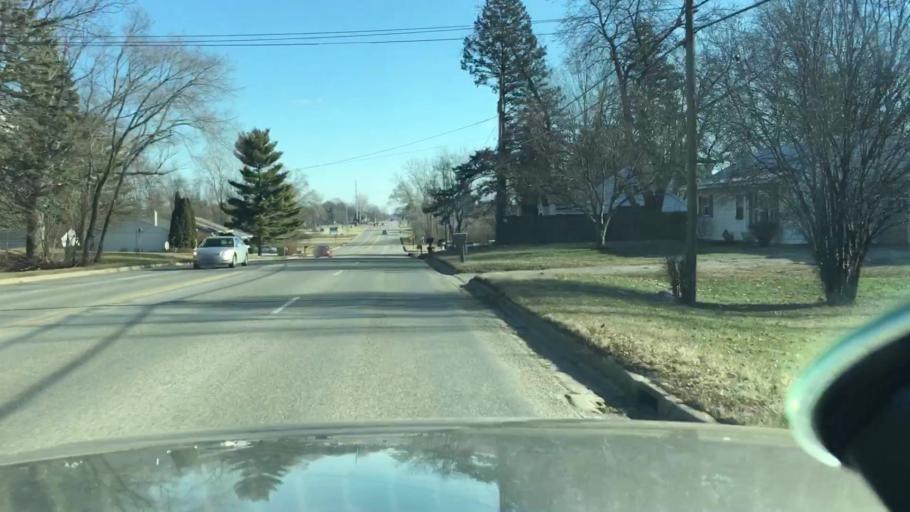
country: US
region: Michigan
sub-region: Jackson County
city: Jackson
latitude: 42.2911
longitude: -84.4271
